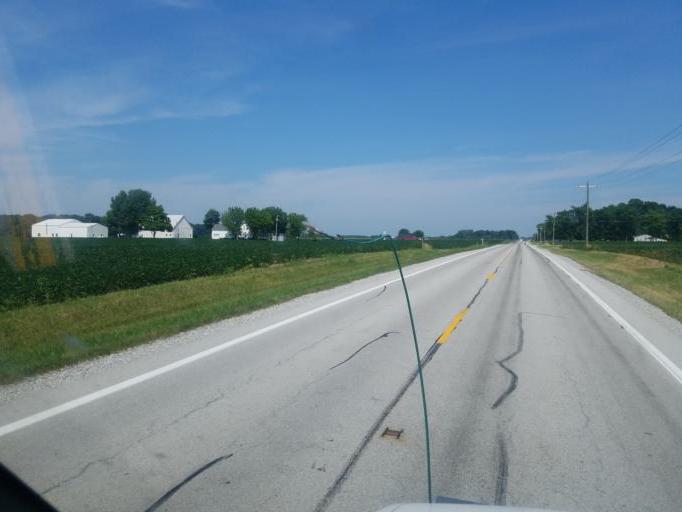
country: US
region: Ohio
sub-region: Shelby County
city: Botkins
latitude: 40.4964
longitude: -84.2721
